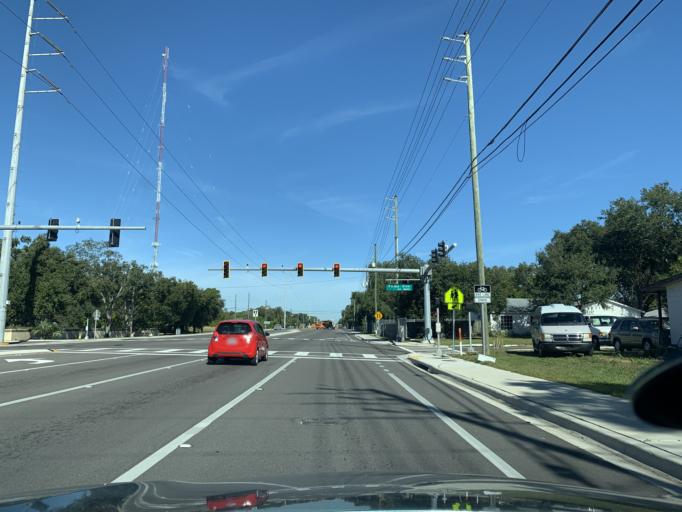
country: US
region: Florida
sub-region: Pinellas County
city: Seminole
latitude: 27.8449
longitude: -82.7622
